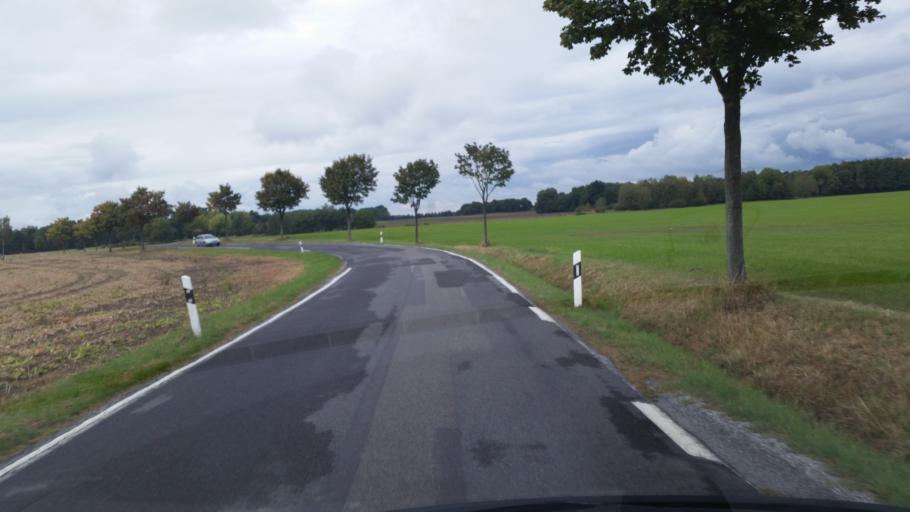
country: DE
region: Saxony
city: Neukirch
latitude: 51.3194
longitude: 14.0251
